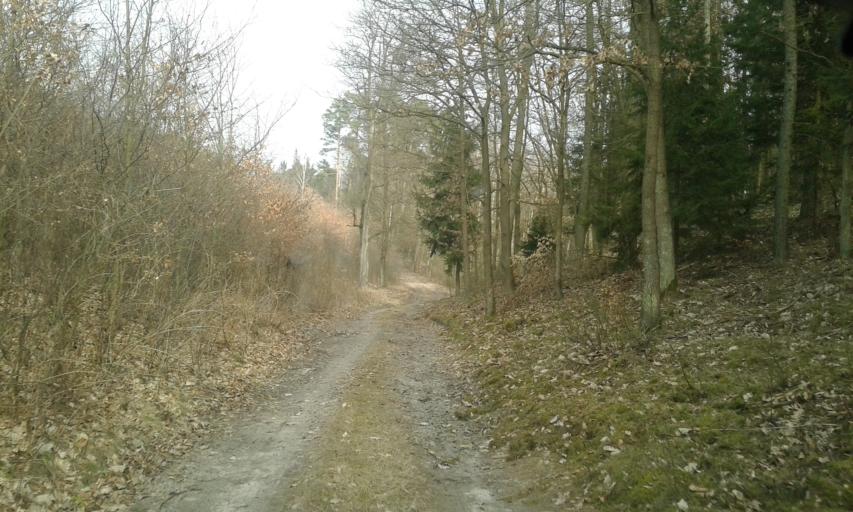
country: PL
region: West Pomeranian Voivodeship
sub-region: Powiat choszczenski
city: Pelczyce
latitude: 53.0868
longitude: 15.2320
